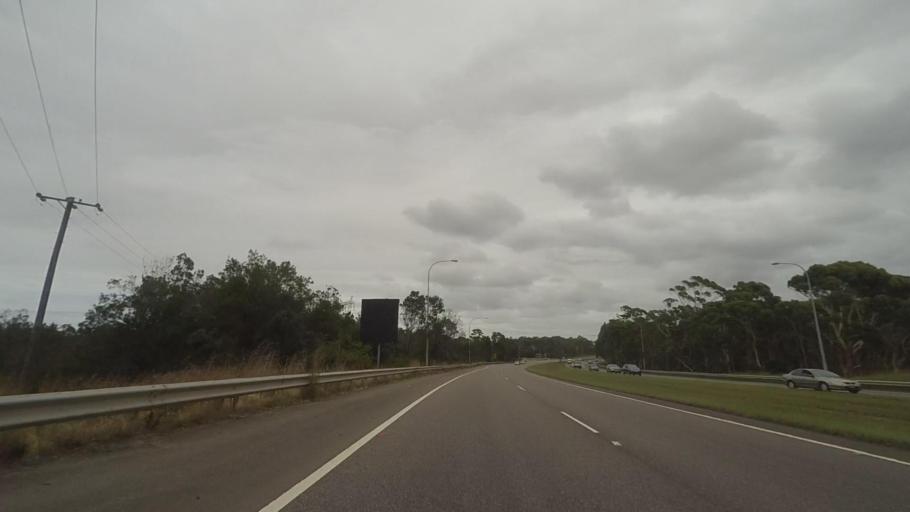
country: AU
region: New South Wales
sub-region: Wyong Shire
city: Buff Point
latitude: -33.2045
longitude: 151.5191
